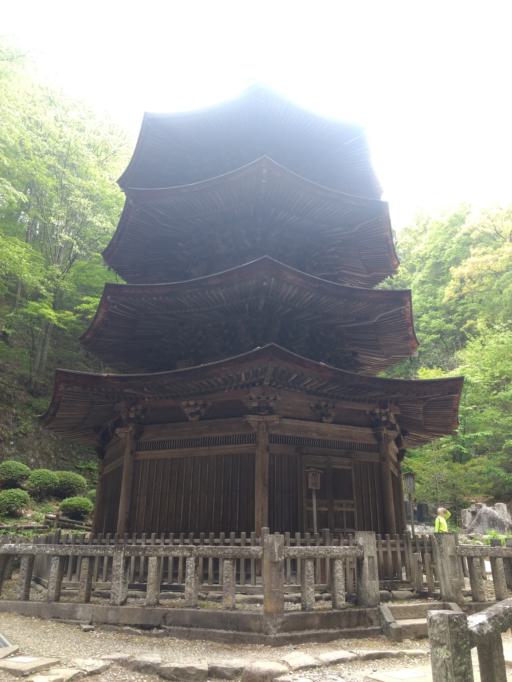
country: JP
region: Nagano
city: Kamimaruko
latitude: 36.3524
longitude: 138.1523
